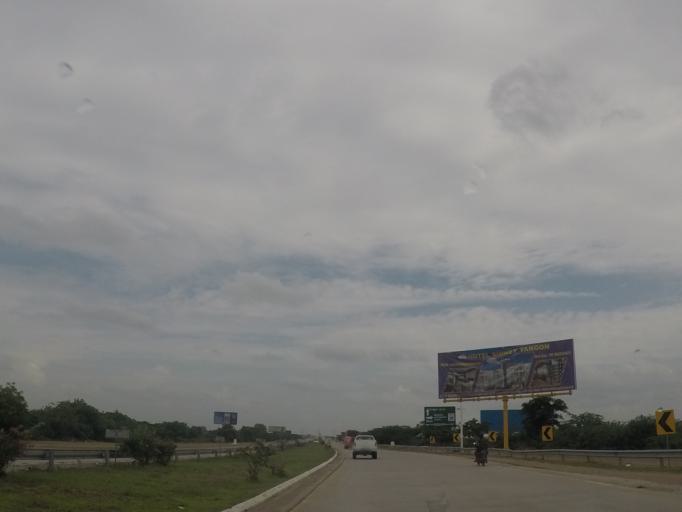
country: MM
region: Sagain
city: Sagaing
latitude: 21.7696
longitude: 95.9713
